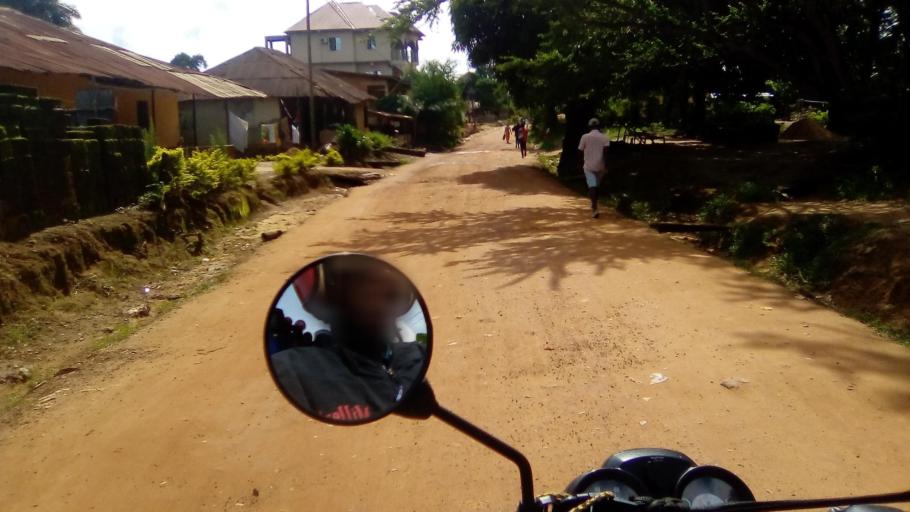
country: SL
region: Southern Province
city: Bo
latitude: 7.9585
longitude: -11.7503
